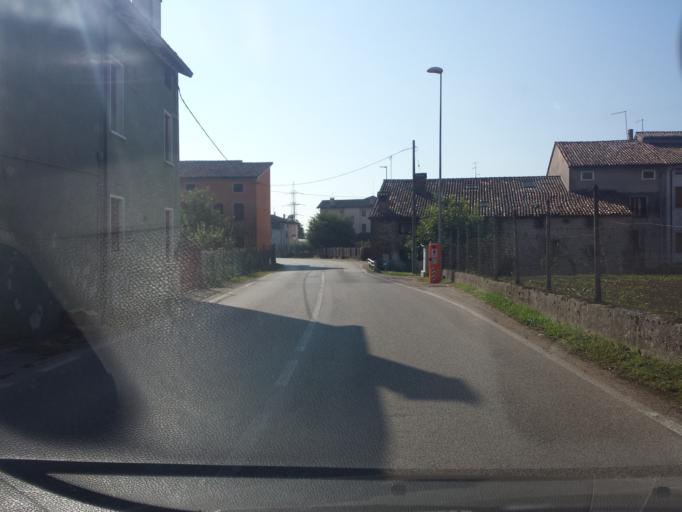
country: IT
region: Veneto
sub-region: Provincia di Vicenza
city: Sandrigo
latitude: 45.6529
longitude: 11.6040
